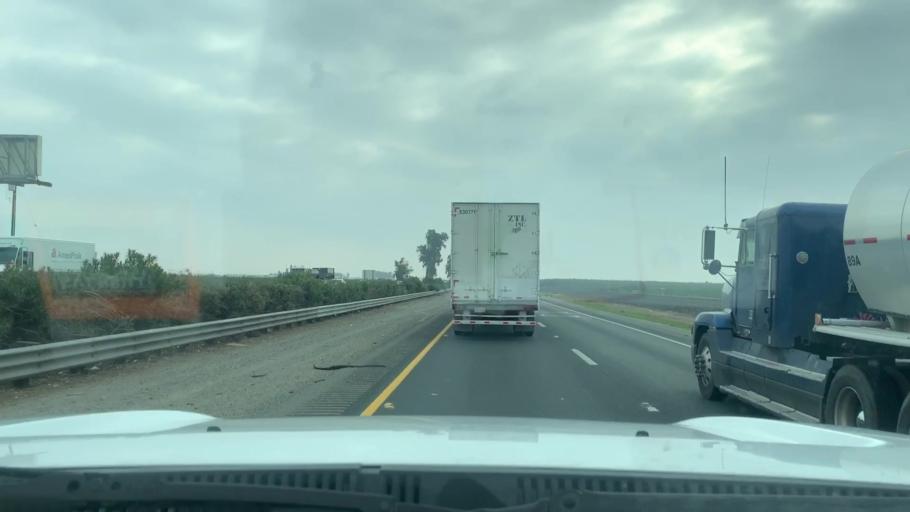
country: US
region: California
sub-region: Tulare County
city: Tipton
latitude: 36.0423
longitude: -119.3106
